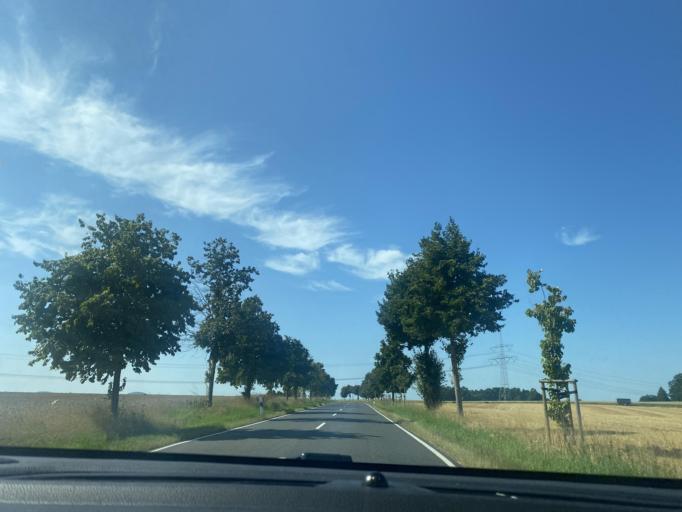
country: DE
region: Saxony
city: Bernstadt
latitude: 51.0343
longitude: 14.8134
